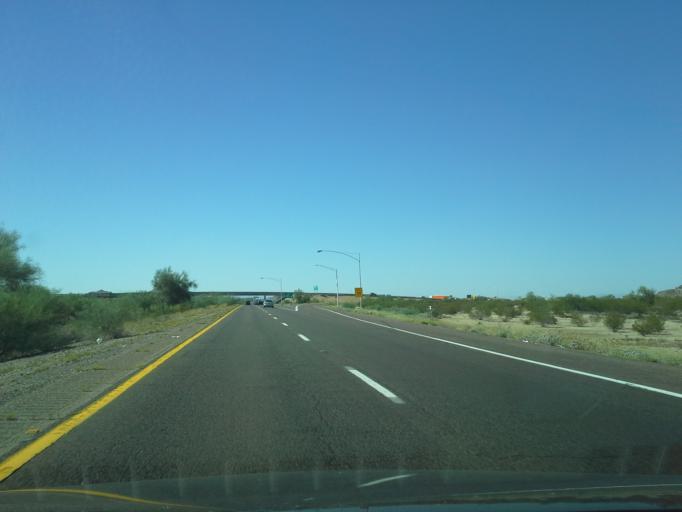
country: US
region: Arizona
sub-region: Pinal County
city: Sacaton
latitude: 33.0004
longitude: -111.7506
